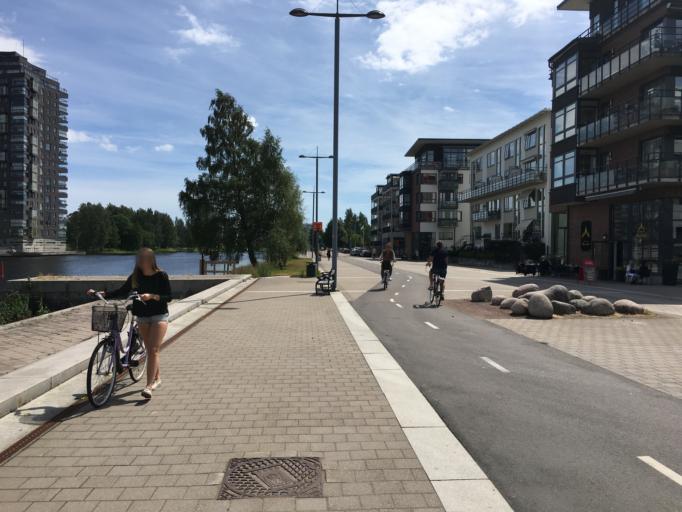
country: SE
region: Vaermland
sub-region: Karlstads Kommun
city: Karlstad
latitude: 59.3757
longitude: 13.5071
